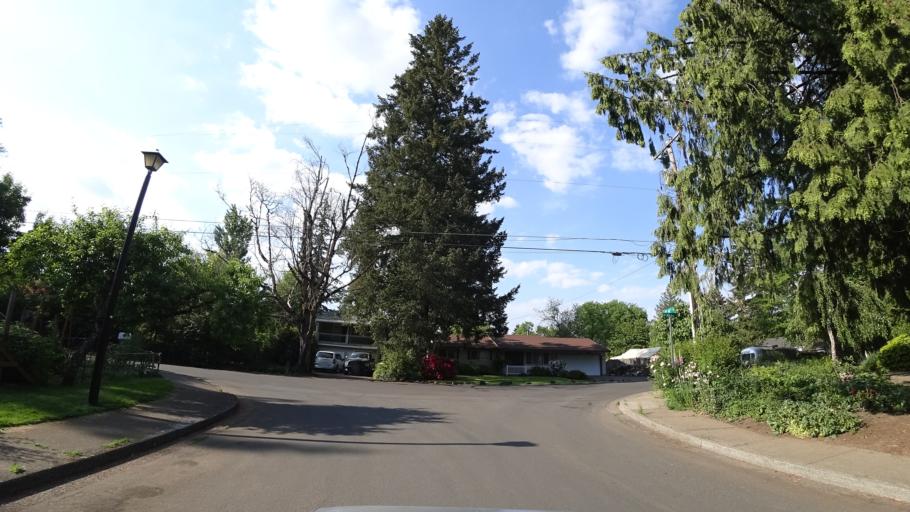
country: US
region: Oregon
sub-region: Washington County
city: Garden Home-Whitford
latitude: 45.4618
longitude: -122.7472
